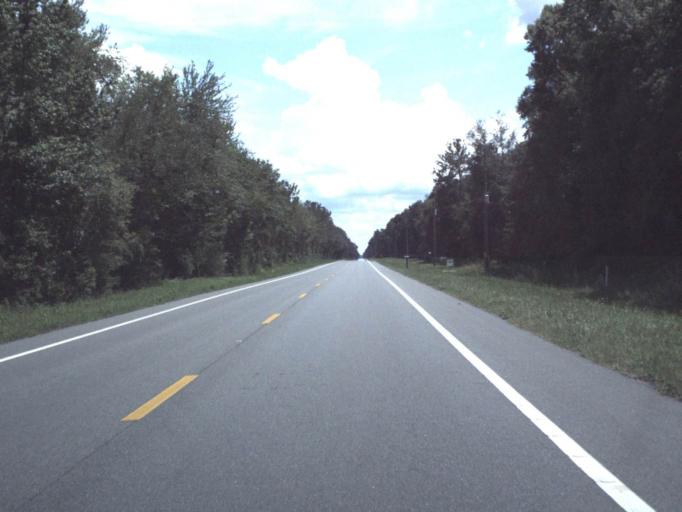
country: US
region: Florida
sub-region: Columbia County
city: Five Points
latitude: 30.4397
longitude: -82.6451
